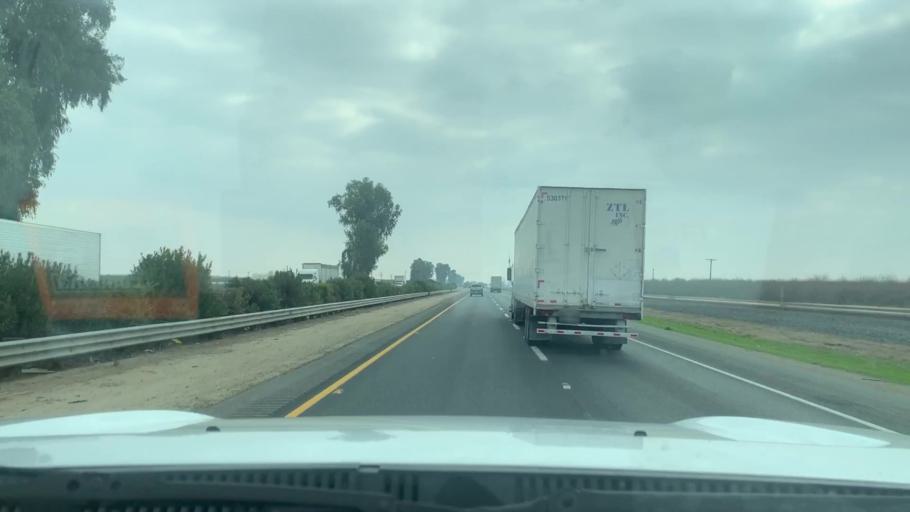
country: US
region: California
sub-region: Tulare County
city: Tipton
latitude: 36.0280
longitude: -119.3073
